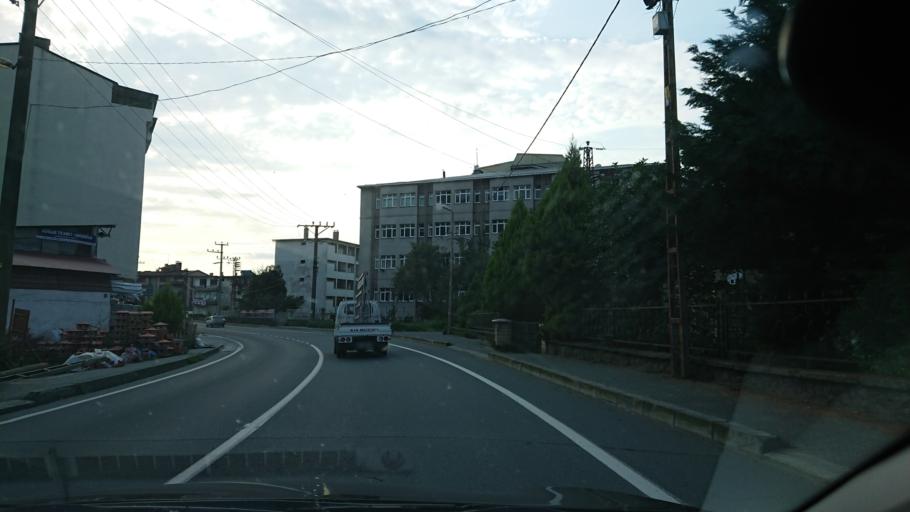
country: TR
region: Rize
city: Cayeli
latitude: 41.0819
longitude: 40.7116
